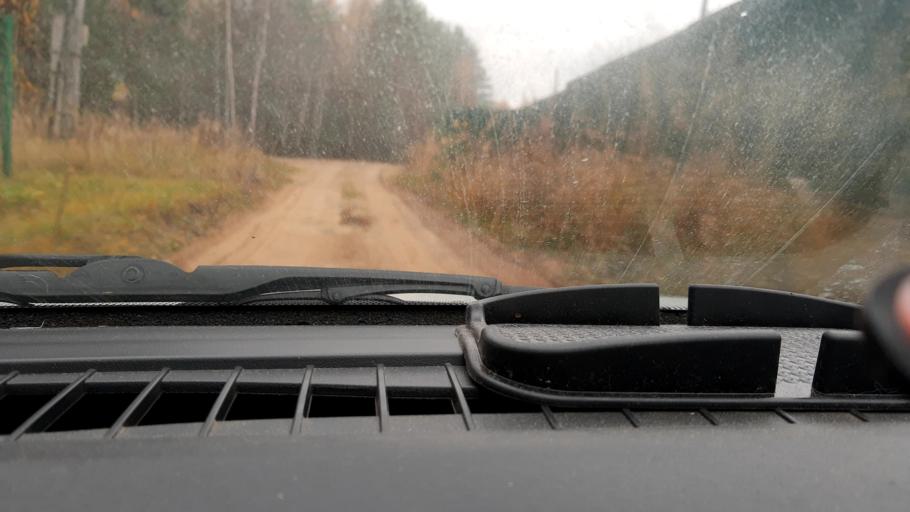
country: RU
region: Nizjnij Novgorod
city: Sitniki
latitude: 56.4258
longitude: 44.0551
